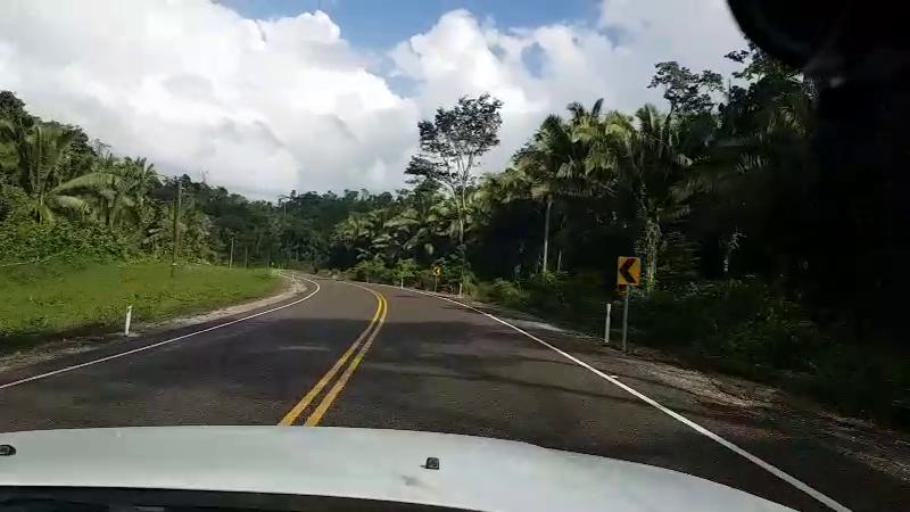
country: BZ
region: Cayo
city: Belmopan
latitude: 17.1488
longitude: -88.7191
